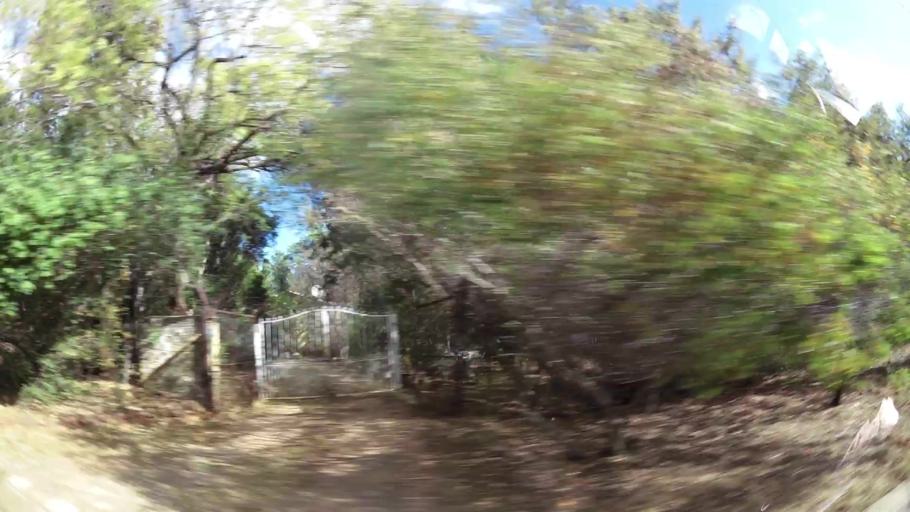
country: ZA
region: Gauteng
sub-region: West Rand District Municipality
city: Muldersdriseloop
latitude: -26.0919
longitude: 27.8523
